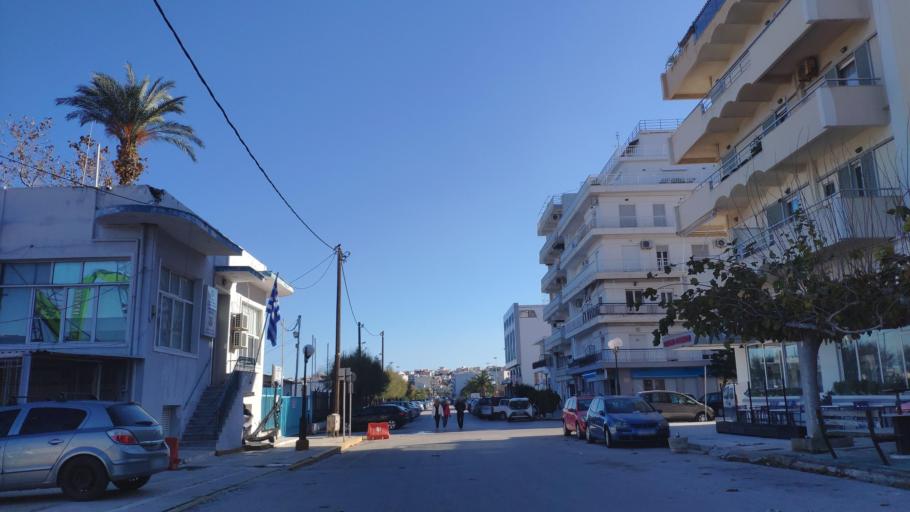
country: GR
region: Peloponnese
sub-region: Nomos Korinthias
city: Korinthos
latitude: 37.9431
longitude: 22.9319
